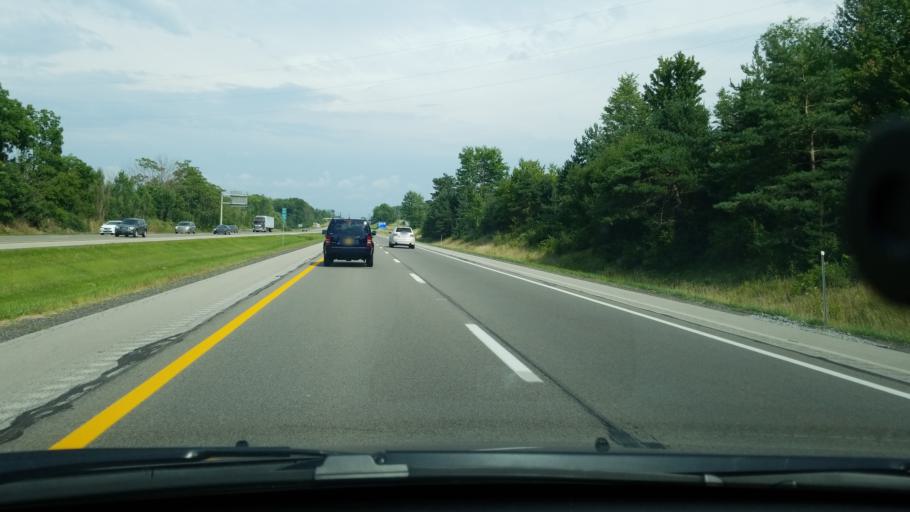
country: US
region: Ohio
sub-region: Mahoning County
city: New Middletown
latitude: 40.9427
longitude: -80.6054
